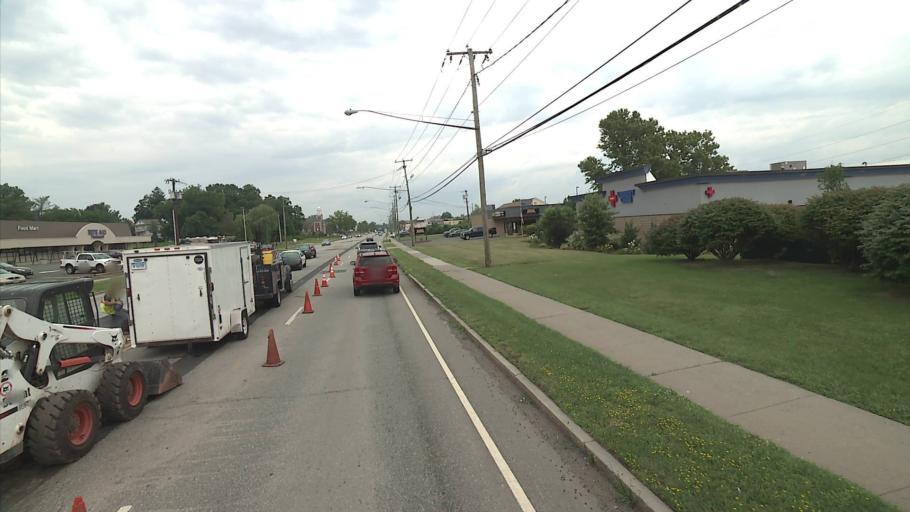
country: US
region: Connecticut
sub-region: Hartford County
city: Wethersfield
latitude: 41.7061
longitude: -72.6614
